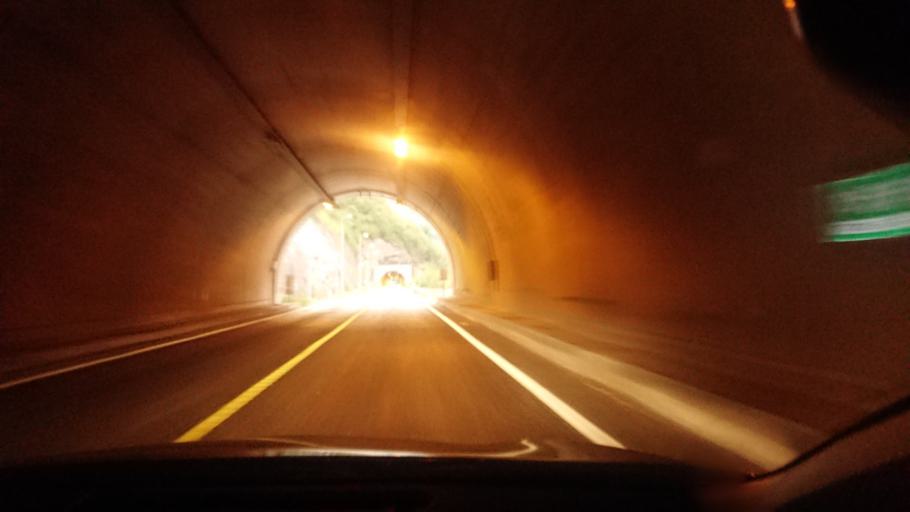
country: TR
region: Karabuk
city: Yenice
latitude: 41.1601
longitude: 32.4796
